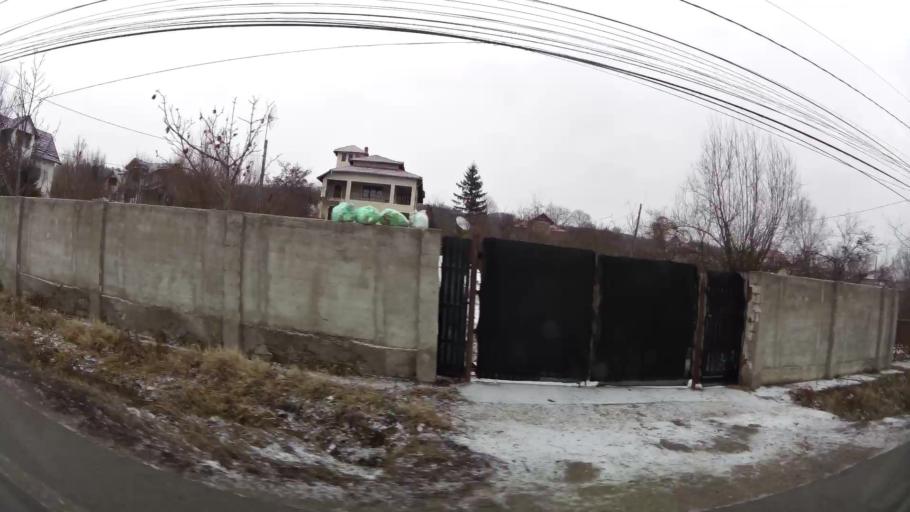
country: RO
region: Dambovita
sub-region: Comuna Aninoasa
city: Viforata
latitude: 44.9507
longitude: 25.4806
